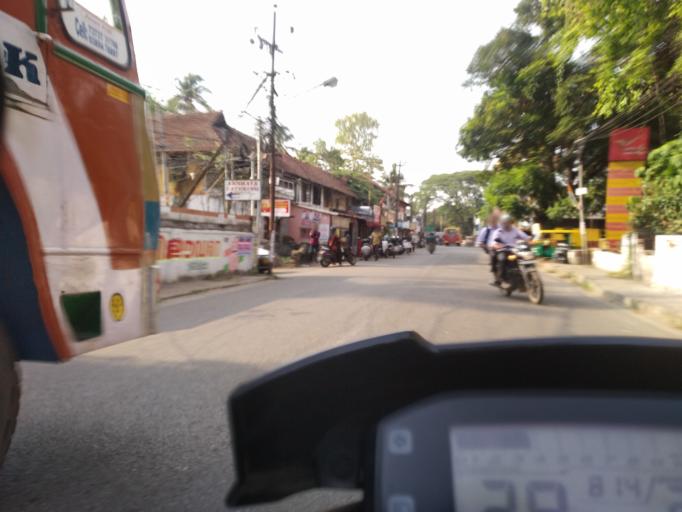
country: IN
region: Kerala
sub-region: Alappuzha
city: Arukutti
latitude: 9.9495
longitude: 76.3470
